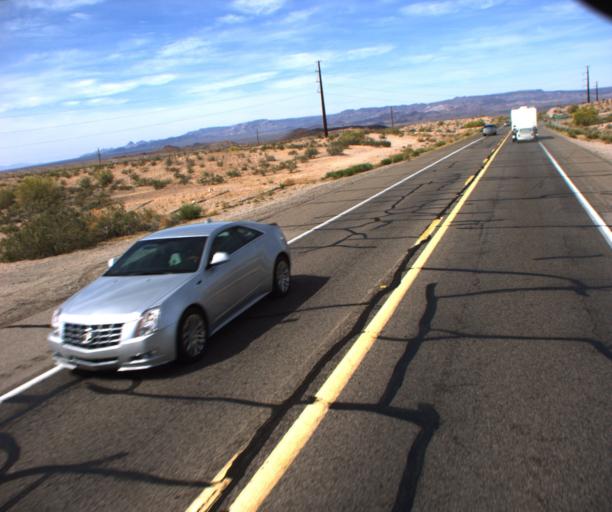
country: US
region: Arizona
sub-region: Mohave County
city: Desert Hills
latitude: 34.6601
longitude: -114.3155
